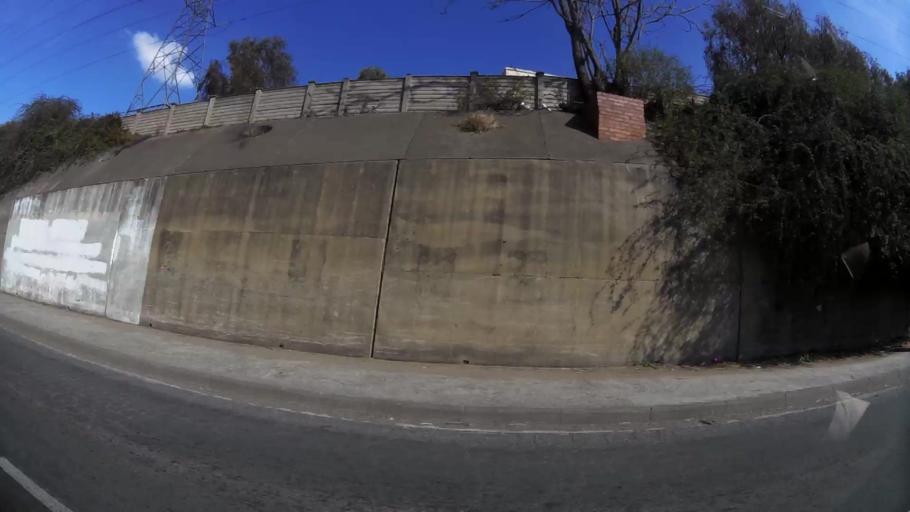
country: ZA
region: Orange Free State
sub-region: Mangaung Metropolitan Municipality
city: Bloemfontein
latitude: -29.1178
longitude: 26.2281
